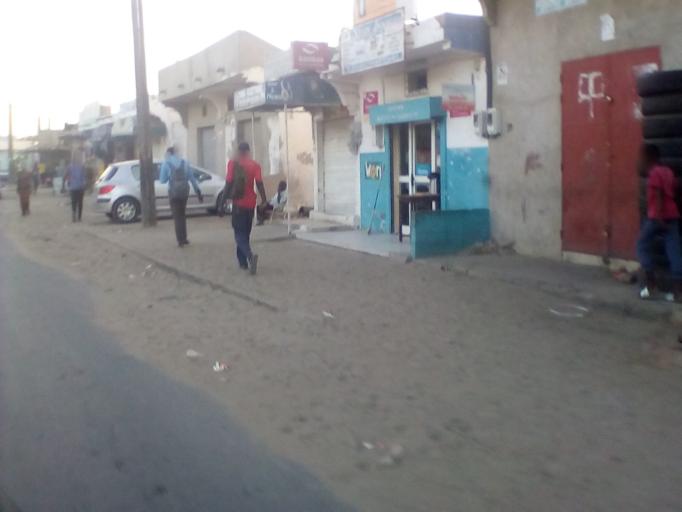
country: SN
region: Saint-Louis
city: Saint-Louis
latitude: 16.0173
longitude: -16.4905
